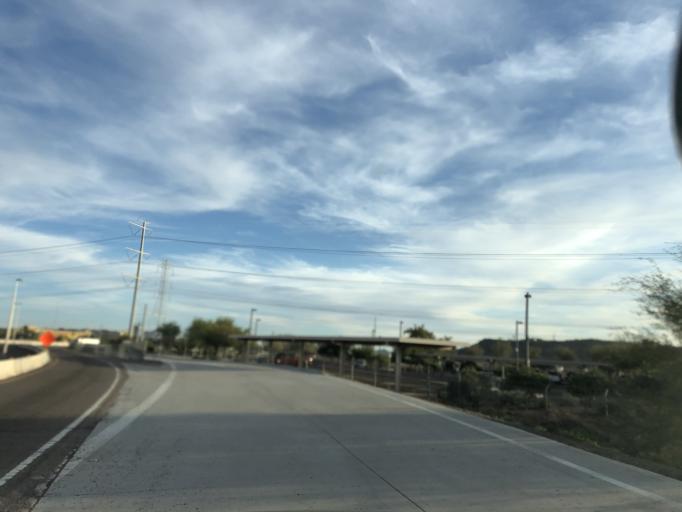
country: US
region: Arizona
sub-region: Maricopa County
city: Anthem
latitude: 33.7113
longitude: -112.1196
